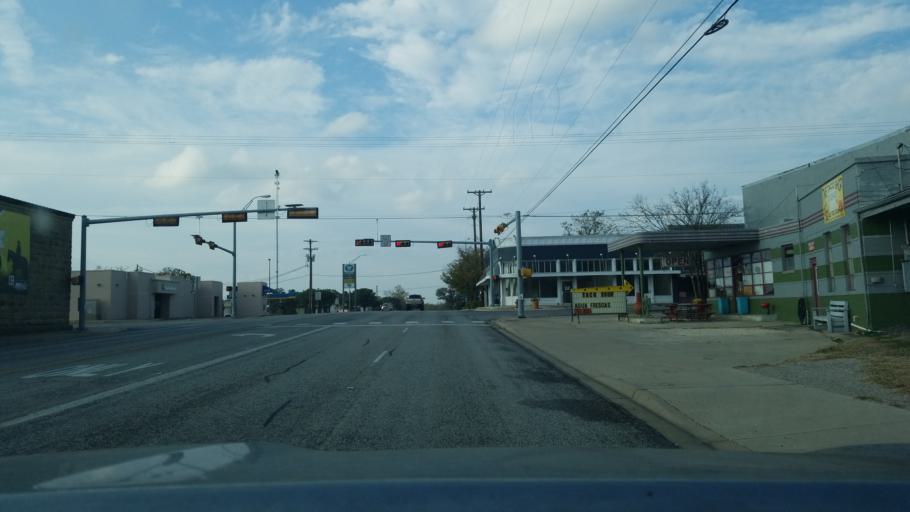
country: US
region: Texas
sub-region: Lampasas County
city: Lampasas
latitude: 31.2161
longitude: -98.3936
